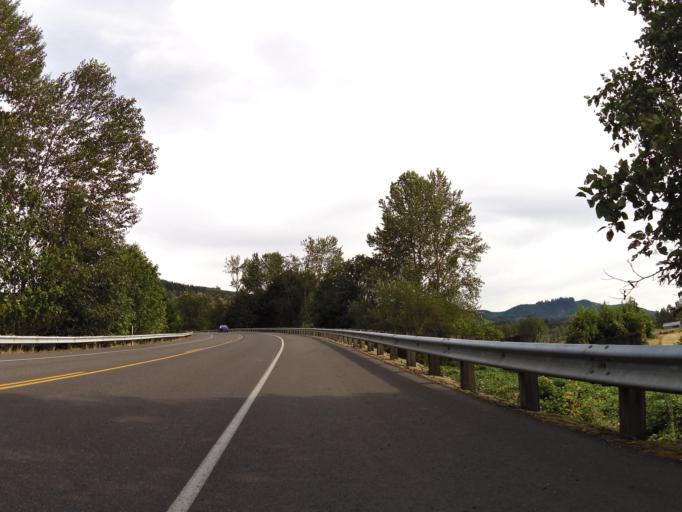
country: US
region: Washington
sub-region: Cowlitz County
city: Castle Rock
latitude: 46.2608
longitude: -122.8923
